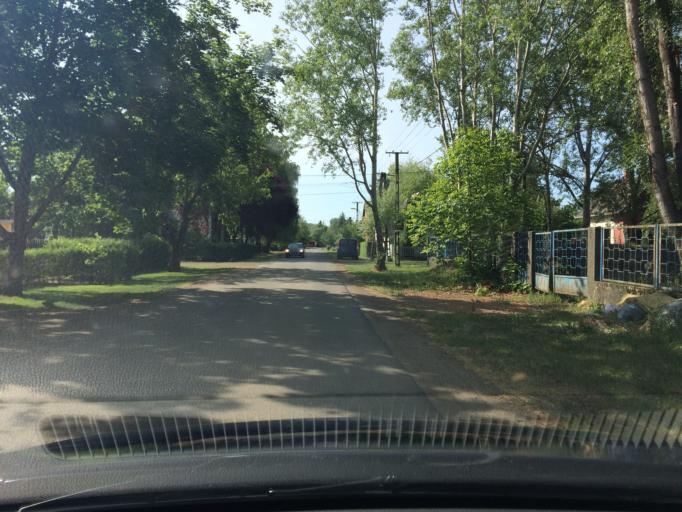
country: HU
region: Szabolcs-Szatmar-Bereg
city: Tiszavasvari
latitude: 47.9565
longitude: 21.3468
